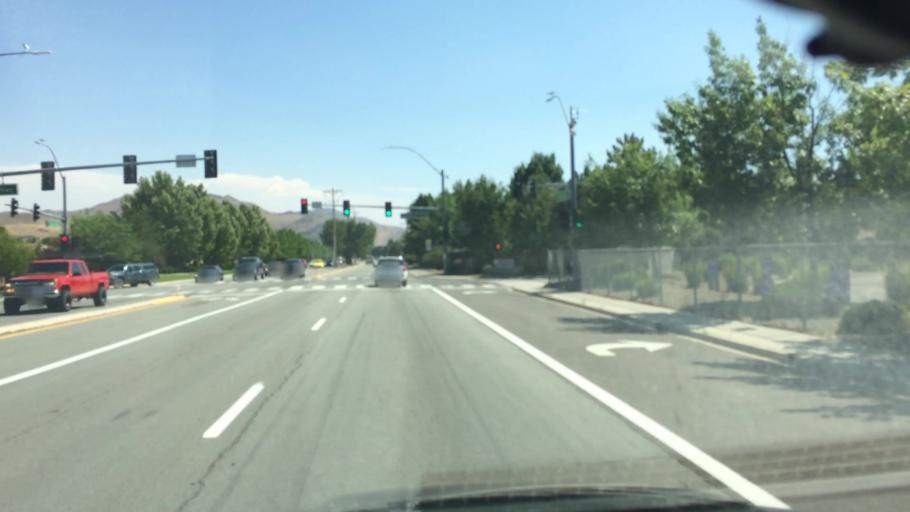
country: US
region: Nevada
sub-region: Washoe County
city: Sparks
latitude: 39.5513
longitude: -119.7058
